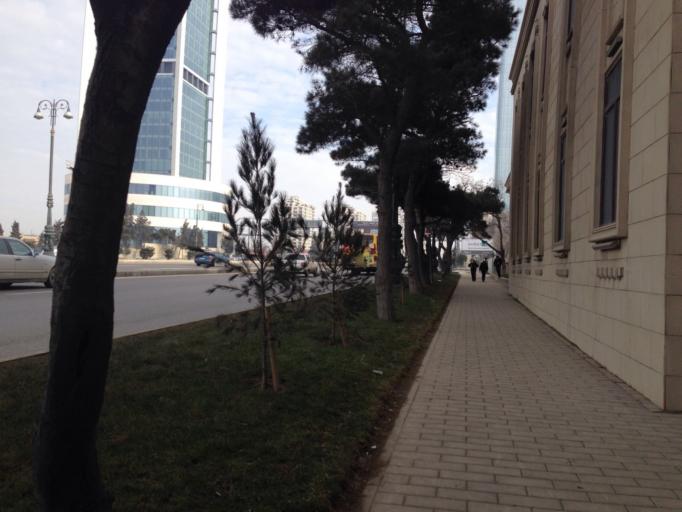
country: AZ
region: Baki
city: Baku
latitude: 40.4132
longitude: 49.9006
